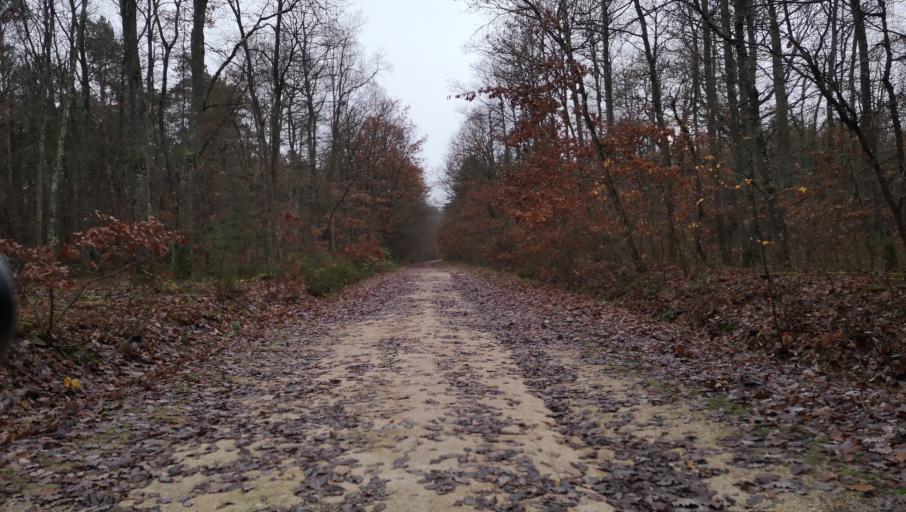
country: FR
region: Centre
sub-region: Departement du Loiret
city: Chanteau
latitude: 47.9436
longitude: 1.9775
